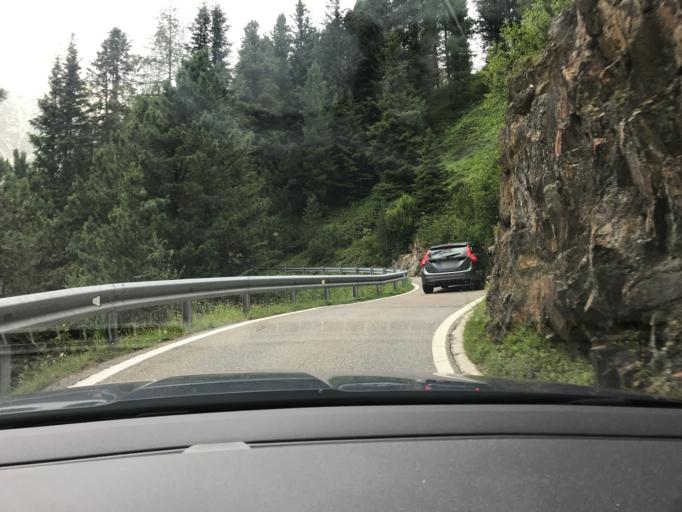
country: IT
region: Trentino-Alto Adige
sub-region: Bolzano
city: San Martino
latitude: 46.8872
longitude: 12.1969
